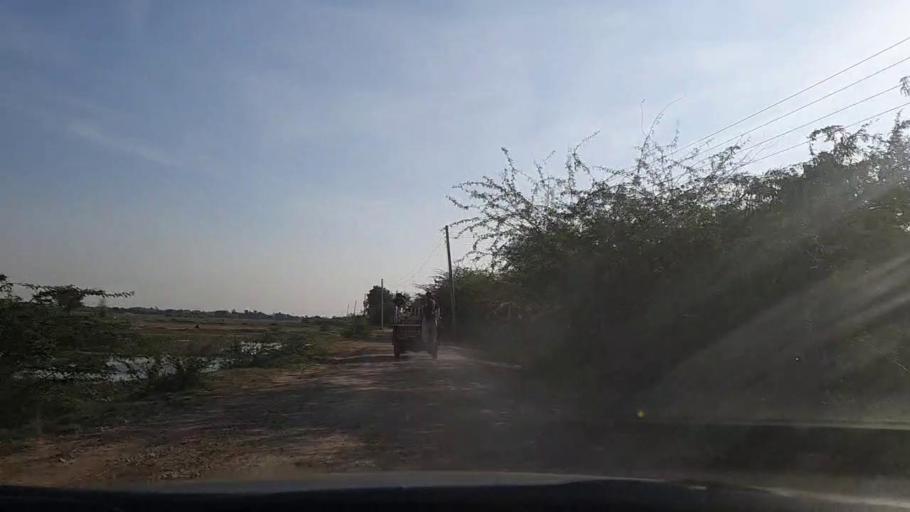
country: PK
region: Sindh
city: Mirpur Sakro
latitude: 24.5329
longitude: 67.6329
